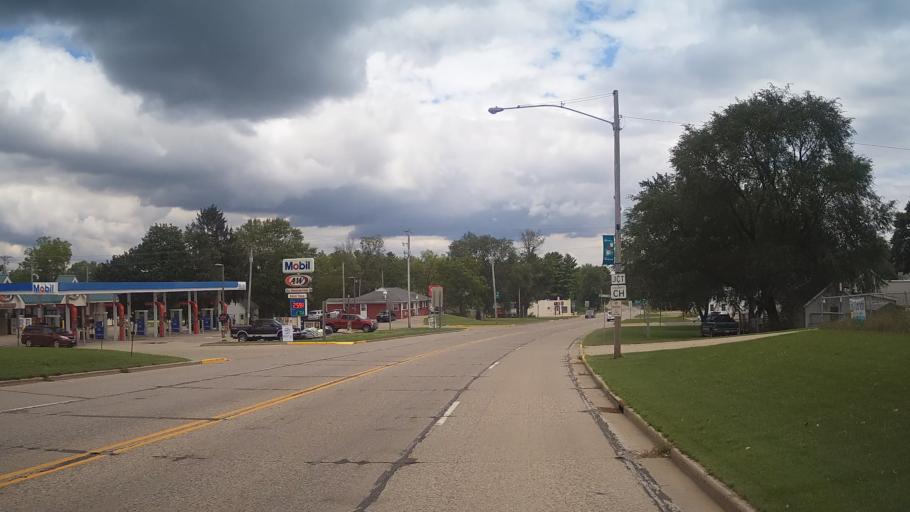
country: US
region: Wisconsin
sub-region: Marquette County
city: Westfield
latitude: 44.0356
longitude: -89.5252
